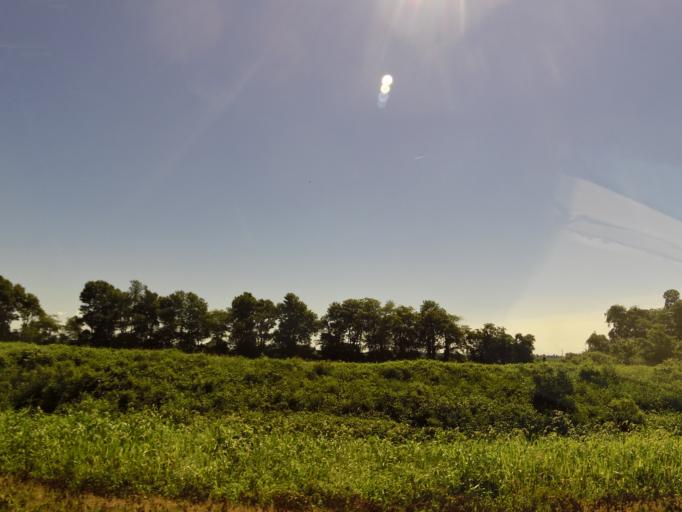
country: US
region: Missouri
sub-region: New Madrid County
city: Lilbourn
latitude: 36.5612
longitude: -89.7027
